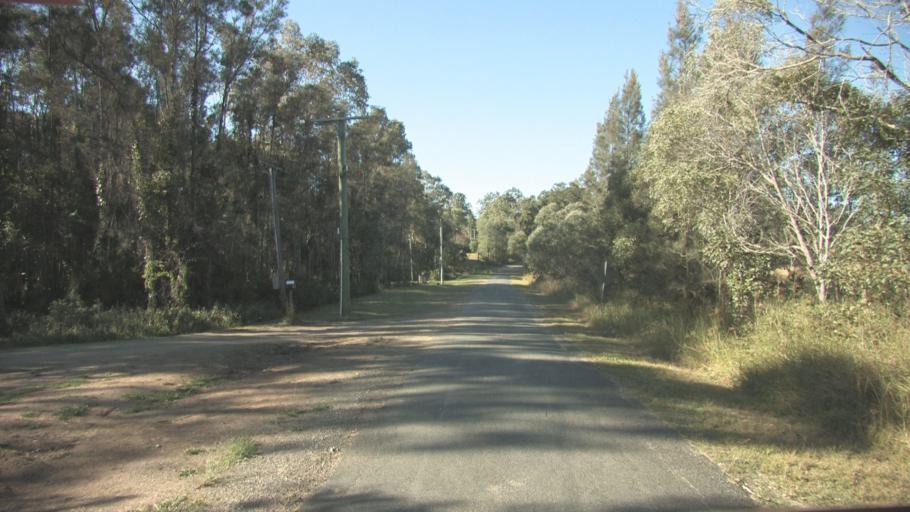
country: AU
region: Queensland
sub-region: Logan
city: Logan Reserve
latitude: -27.7360
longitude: 153.0953
